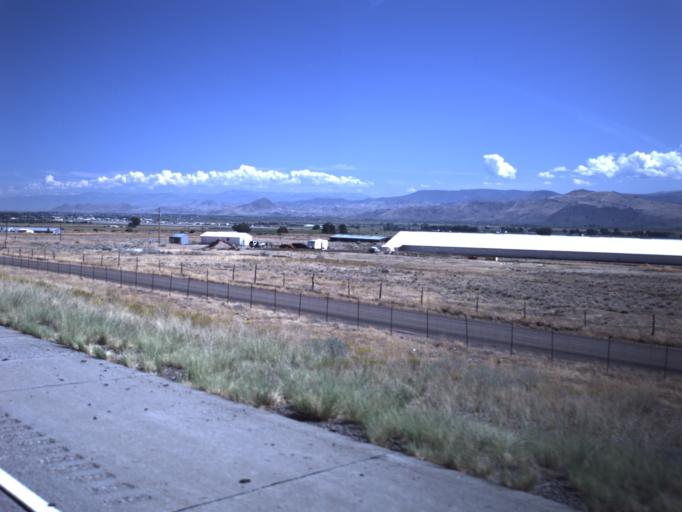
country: US
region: Utah
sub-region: Sevier County
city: Monroe
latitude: 38.7101
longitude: -112.1373
